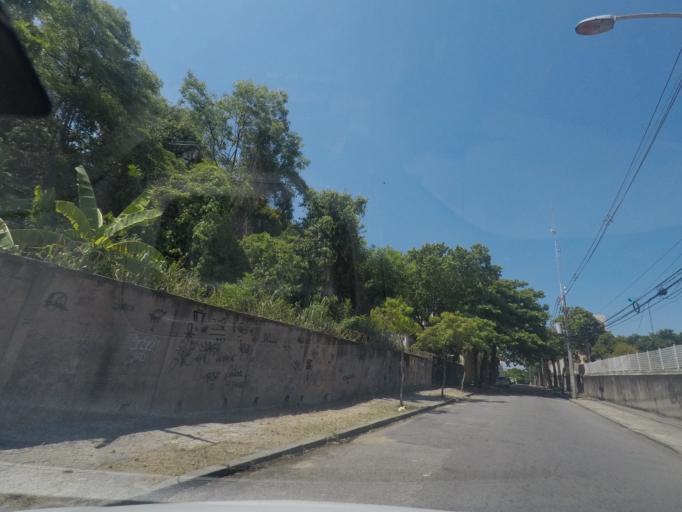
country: BR
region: Rio de Janeiro
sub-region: Rio De Janeiro
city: Rio de Janeiro
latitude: -22.8968
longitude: -43.2236
